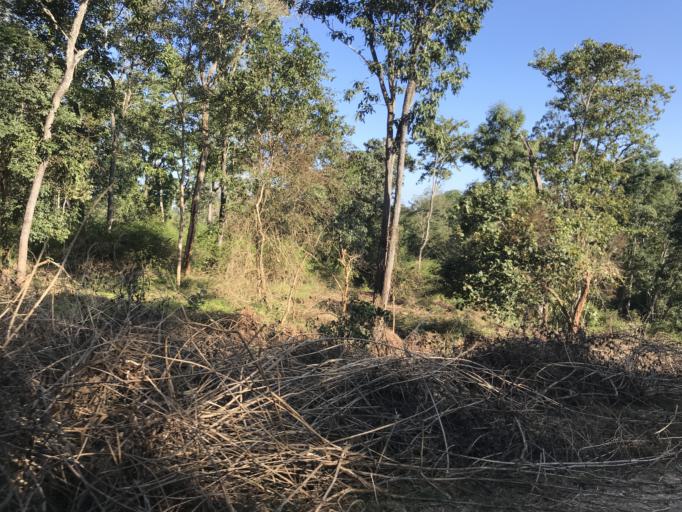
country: IN
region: Karnataka
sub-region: Mysore
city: Heggadadevankote
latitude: 11.9813
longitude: 76.2331
